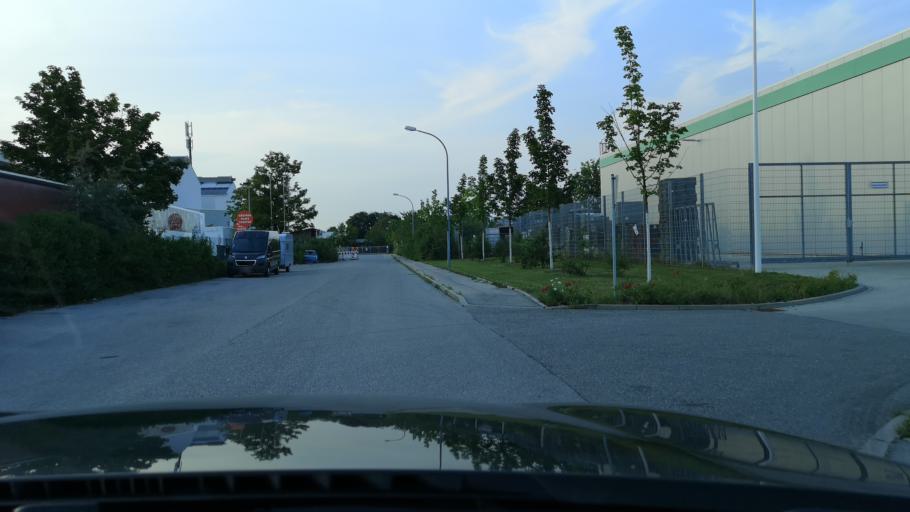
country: DE
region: Bavaria
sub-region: Upper Bavaria
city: Poing
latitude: 48.1704
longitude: 11.7964
